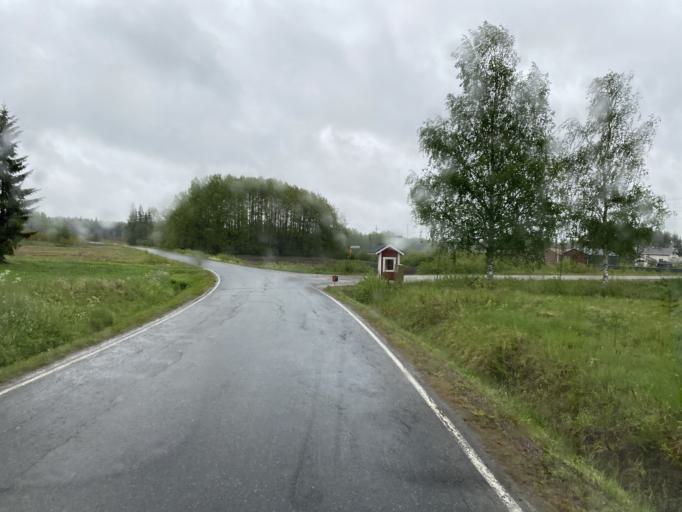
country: FI
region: Pirkanmaa
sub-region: Etelae-Pirkanmaa
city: Urjala
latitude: 60.9750
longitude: 23.5438
